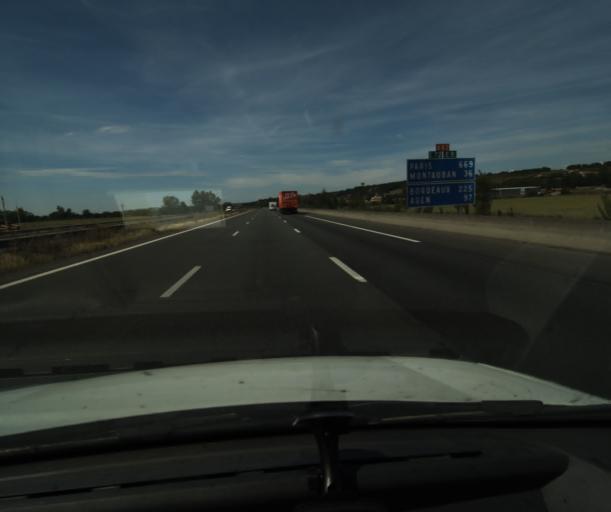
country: FR
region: Midi-Pyrenees
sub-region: Departement de la Haute-Garonne
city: Bruguieres
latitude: 43.7264
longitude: 1.3992
